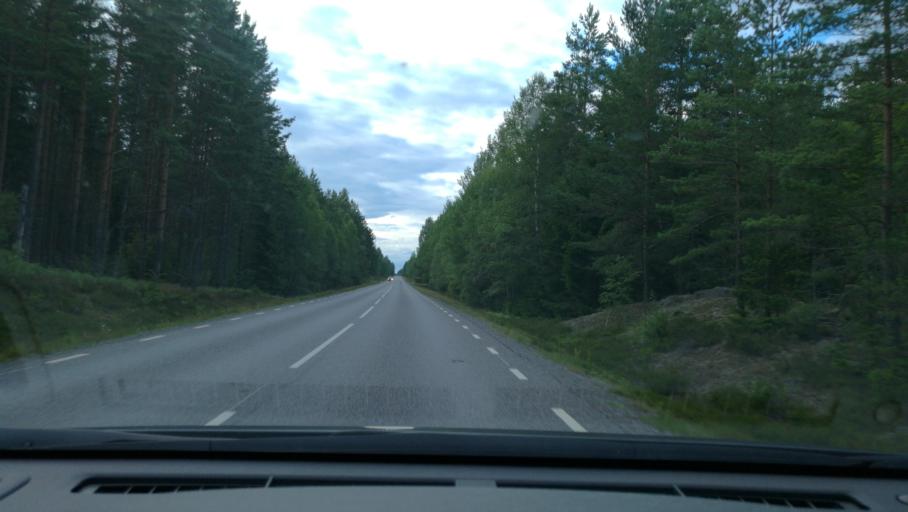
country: SE
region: OEstergoetland
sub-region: Norrkopings Kommun
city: Svartinge
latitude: 58.7554
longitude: 15.9790
